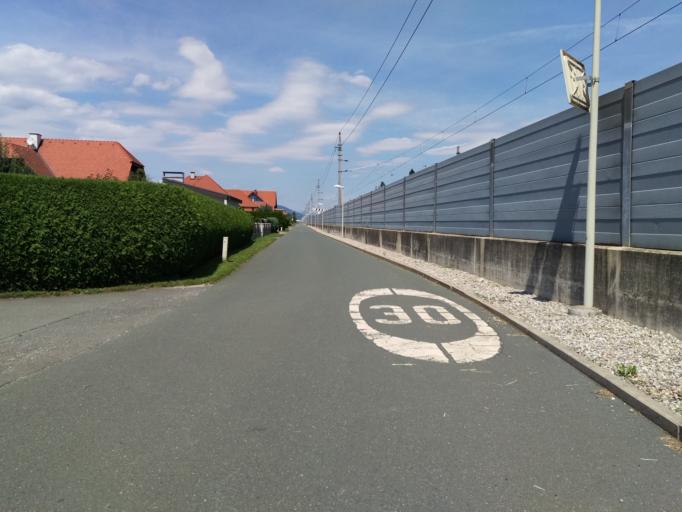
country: AT
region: Styria
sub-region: Politischer Bezirk Graz-Umgebung
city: Gossendorf
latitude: 46.9881
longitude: 15.4554
